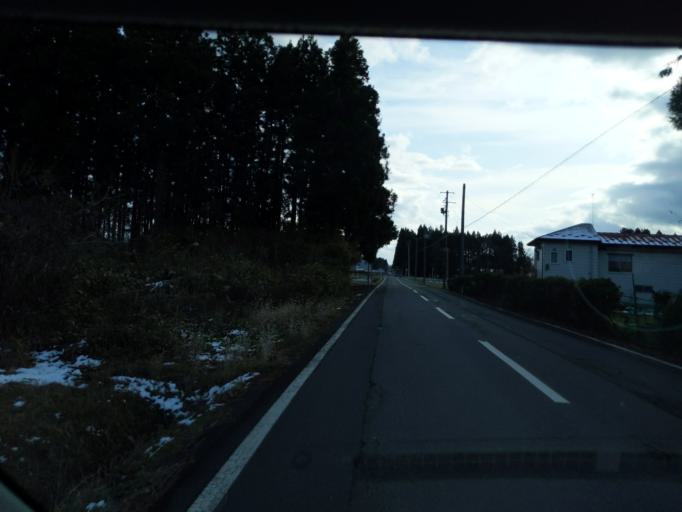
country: JP
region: Iwate
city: Mizusawa
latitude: 39.1109
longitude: 141.0823
